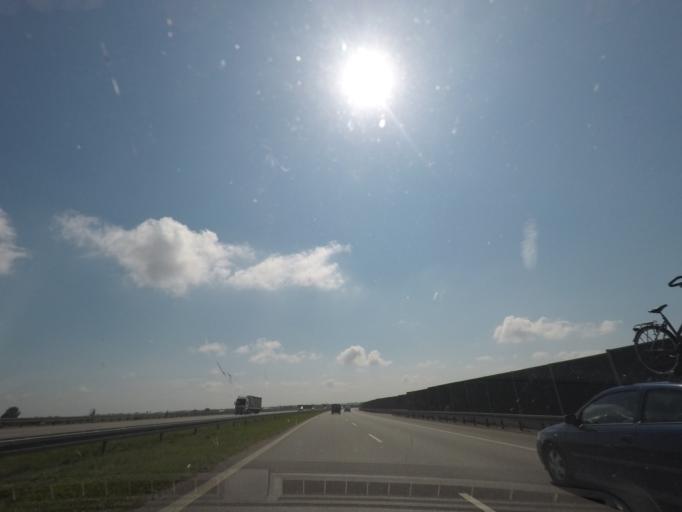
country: PL
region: Kujawsko-Pomorskie
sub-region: Powiat wloclawski
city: Czerniewice
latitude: 52.5243
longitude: 19.0966
